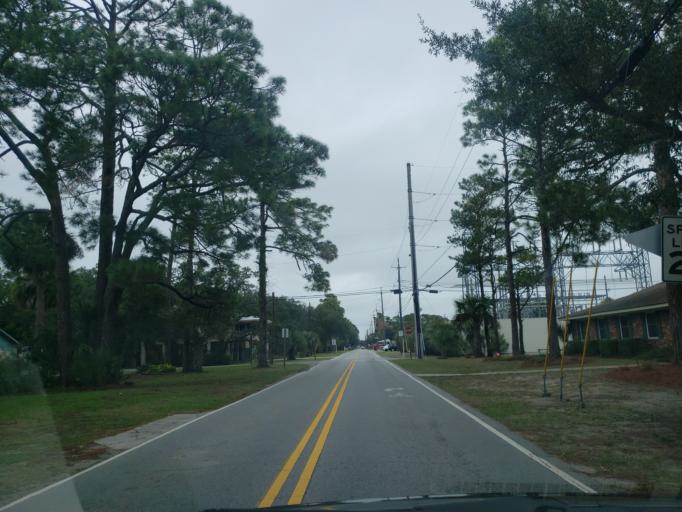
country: US
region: Georgia
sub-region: Chatham County
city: Tybee Island
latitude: 32.0067
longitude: -80.8458
